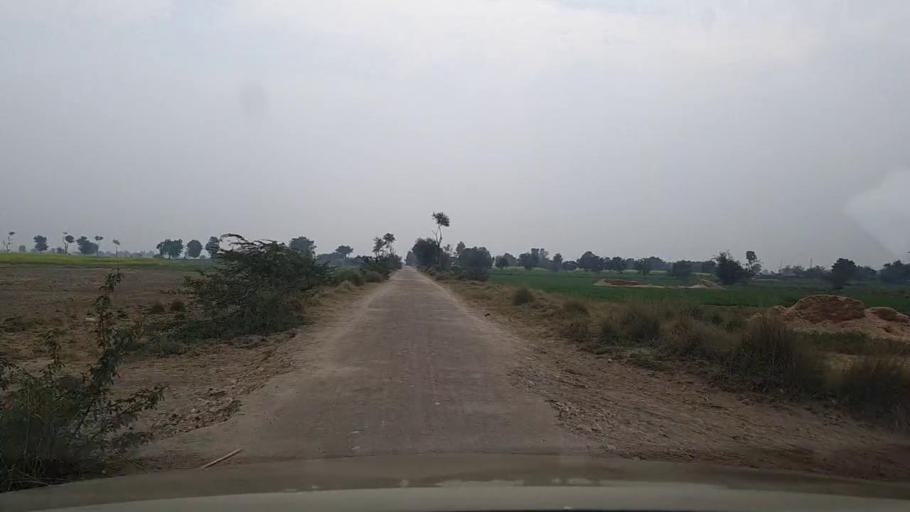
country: PK
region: Sindh
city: Sanghar
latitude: 26.1161
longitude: 68.9043
